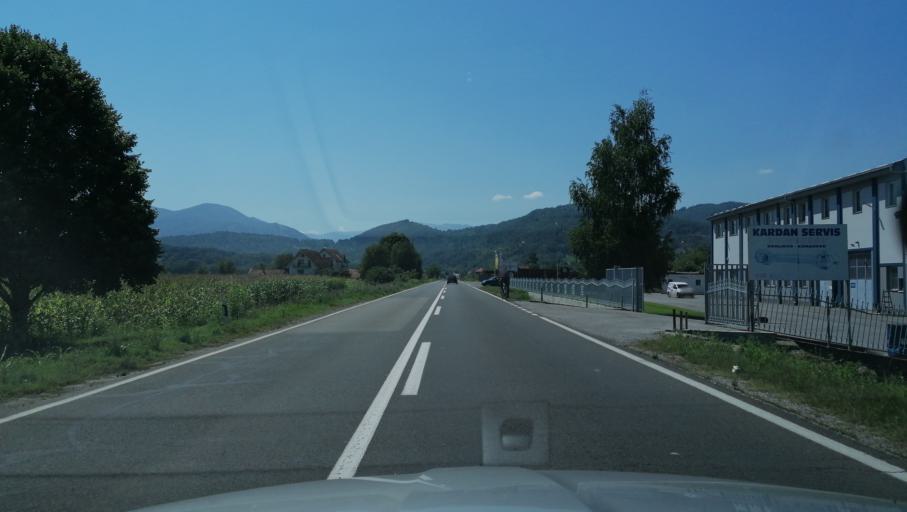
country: RS
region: Central Serbia
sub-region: Raski Okrug
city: Kraljevo
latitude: 43.6925
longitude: 20.5811
